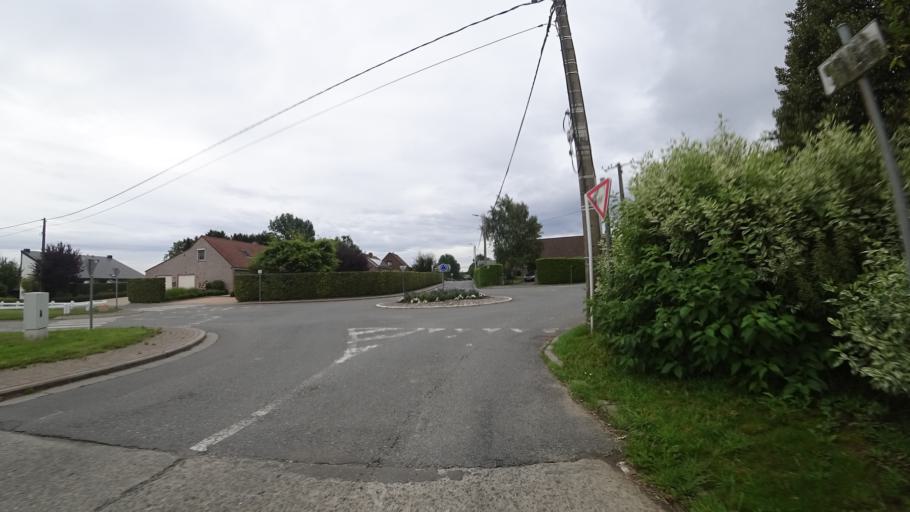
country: BE
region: Wallonia
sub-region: Province du Brabant Wallon
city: Perwez
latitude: 50.5577
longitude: 4.7954
